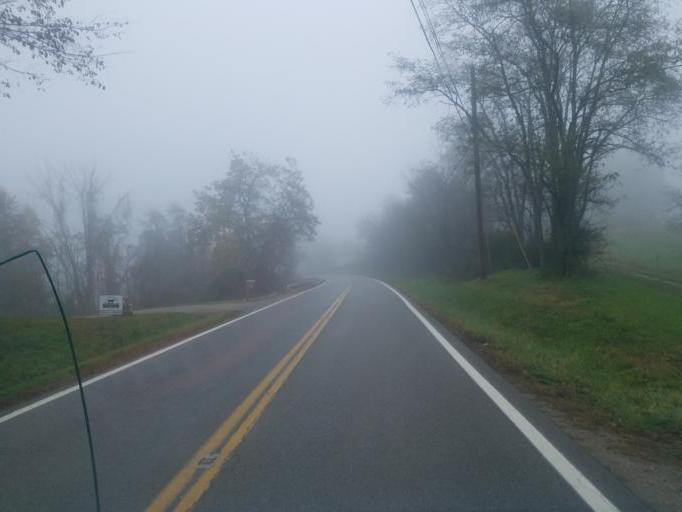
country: US
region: Ohio
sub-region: Morgan County
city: McConnelsville
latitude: 39.6298
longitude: -81.8778
